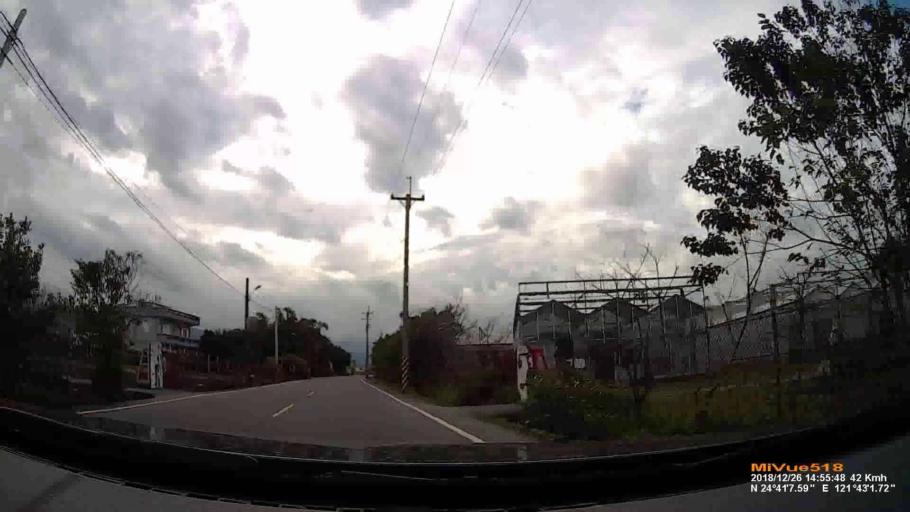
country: TW
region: Taiwan
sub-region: Yilan
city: Yilan
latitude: 24.6855
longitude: 121.7172
